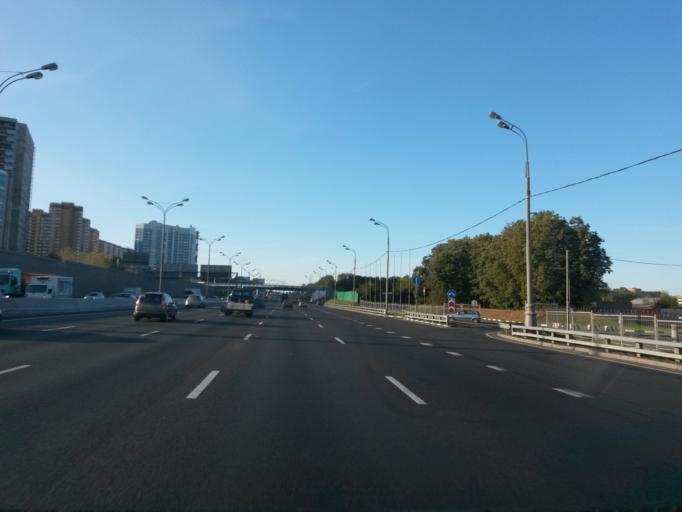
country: RU
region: Moscow
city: Vostochnyy
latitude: 55.8103
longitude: 37.8389
